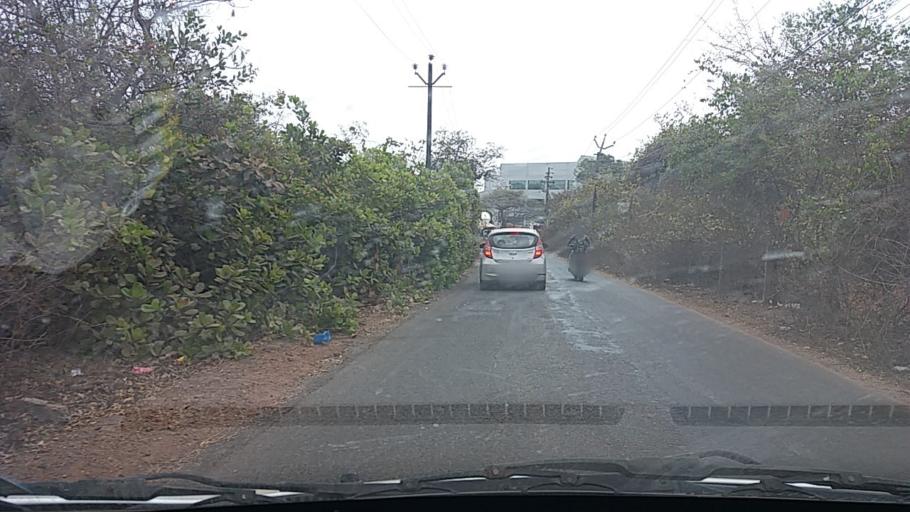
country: IN
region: Goa
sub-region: North Goa
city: Saligao
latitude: 15.5339
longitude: 73.7962
